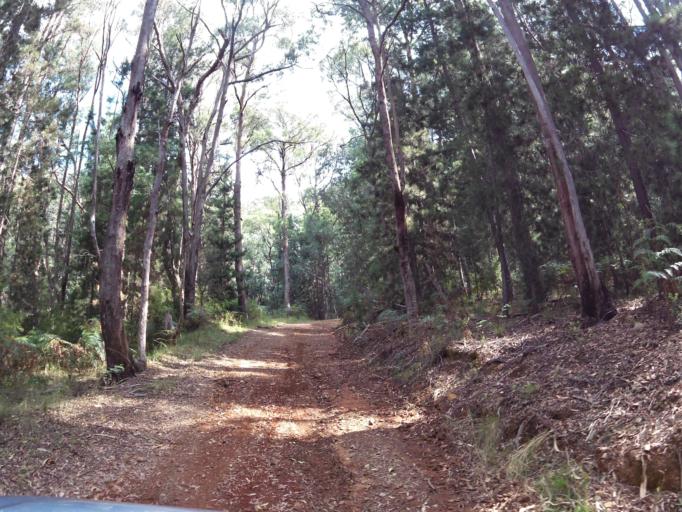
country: AU
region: Victoria
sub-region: Alpine
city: Mount Beauty
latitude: -36.7673
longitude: 147.0149
